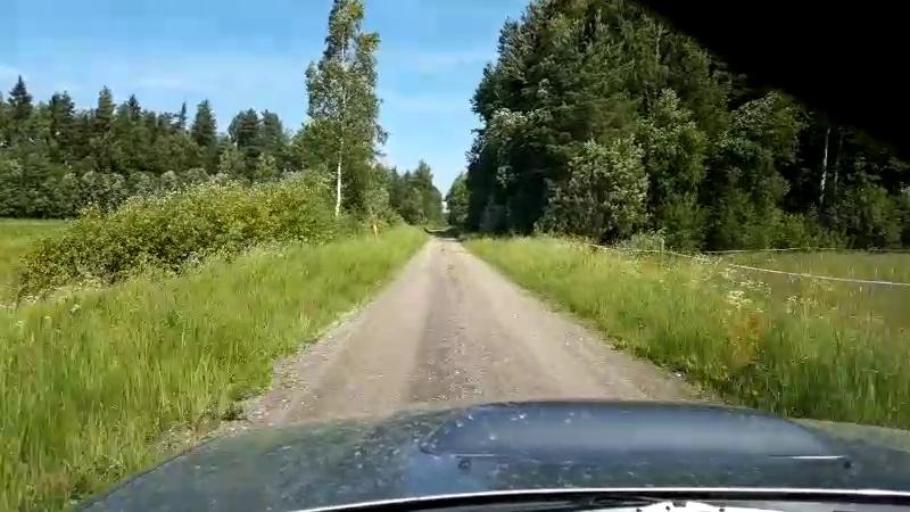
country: EE
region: Paernumaa
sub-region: Sindi linn
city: Sindi
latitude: 58.5195
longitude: 24.6611
